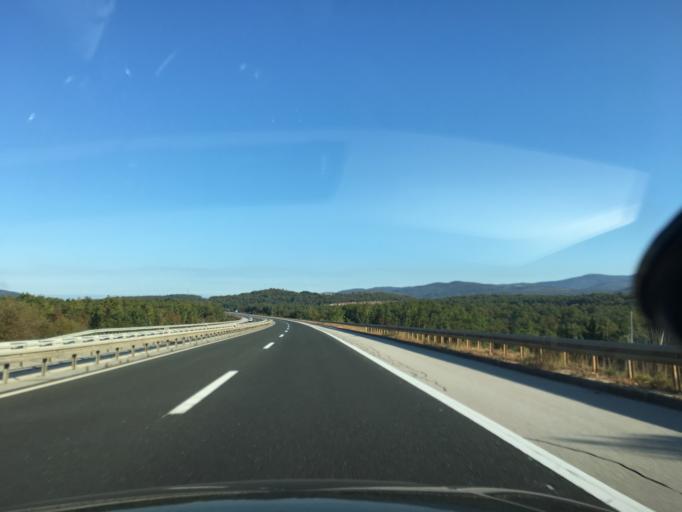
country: HR
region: Licko-Senjska
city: Gospic
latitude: 44.7231
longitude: 15.3861
